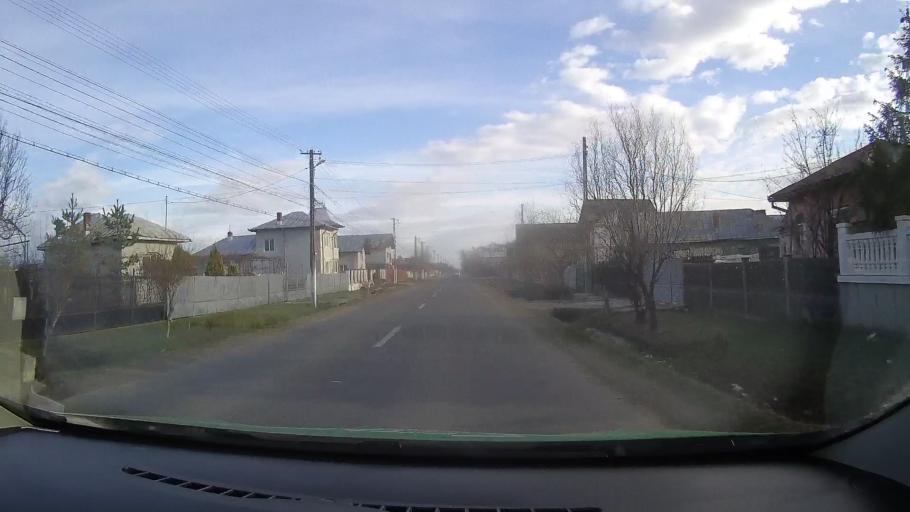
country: RO
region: Dambovita
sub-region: Comuna Vacaresti
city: Vacaresti
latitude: 44.8613
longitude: 25.4793
